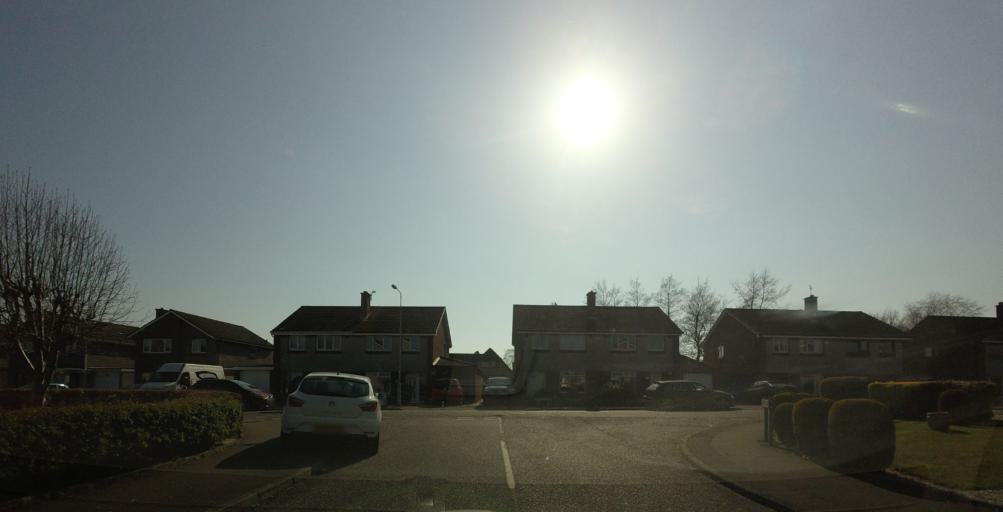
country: GB
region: Scotland
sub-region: Fife
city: Crossford
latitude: 56.0596
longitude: -3.4988
